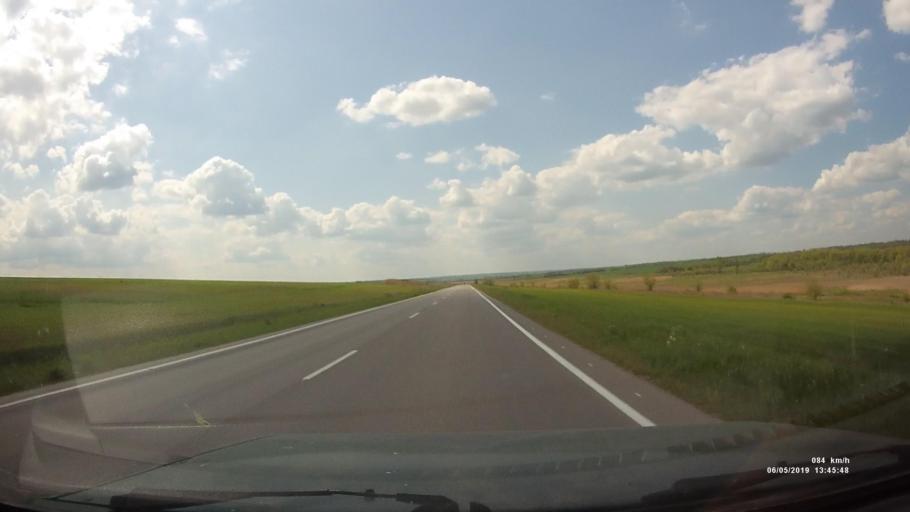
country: RU
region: Rostov
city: Melikhovskaya
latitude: 47.6575
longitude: 40.5935
